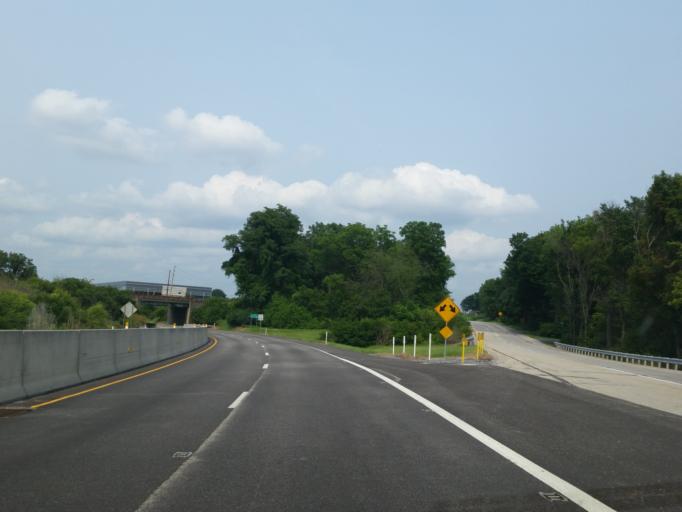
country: US
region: Pennsylvania
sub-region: Cumberland County
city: Camp Hill
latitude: 40.2495
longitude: -76.9212
